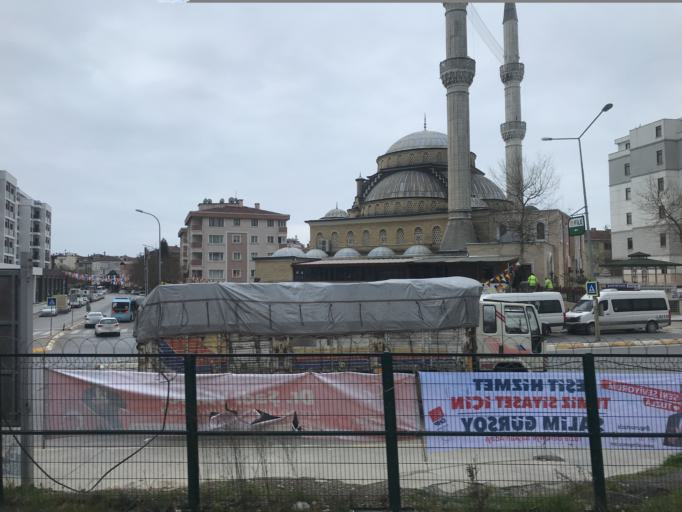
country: TR
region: Istanbul
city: Icmeler
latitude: 40.8410
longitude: 29.3067
